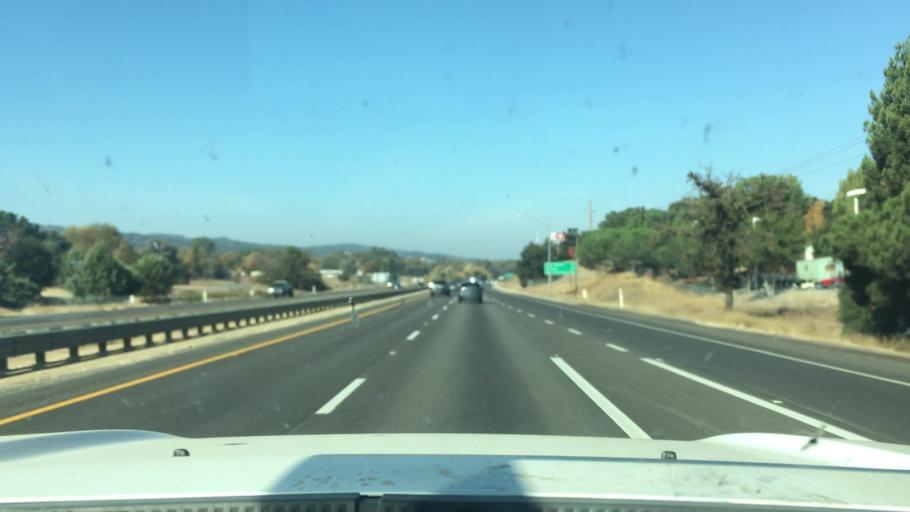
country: US
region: California
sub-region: San Luis Obispo County
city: Atascadero
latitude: 35.4989
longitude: -120.6853
